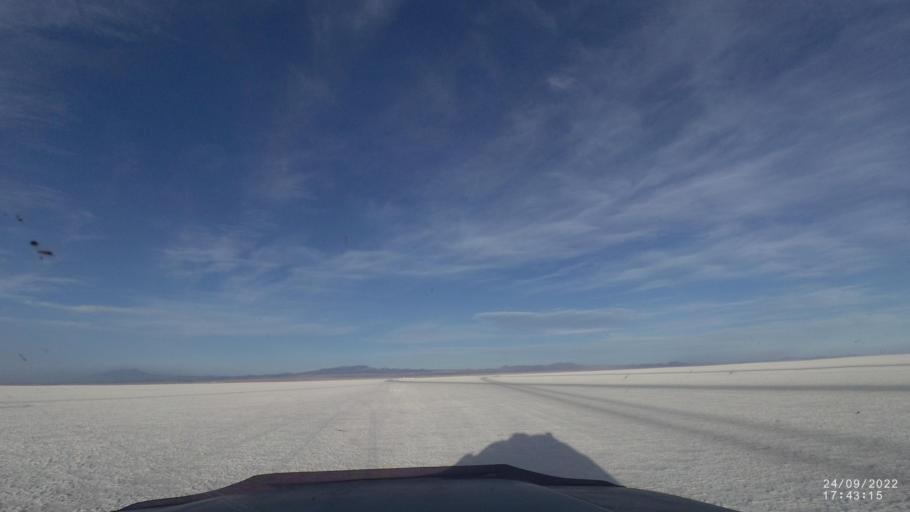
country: BO
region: Potosi
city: Colchani
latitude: -20.3340
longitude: -67.0629
